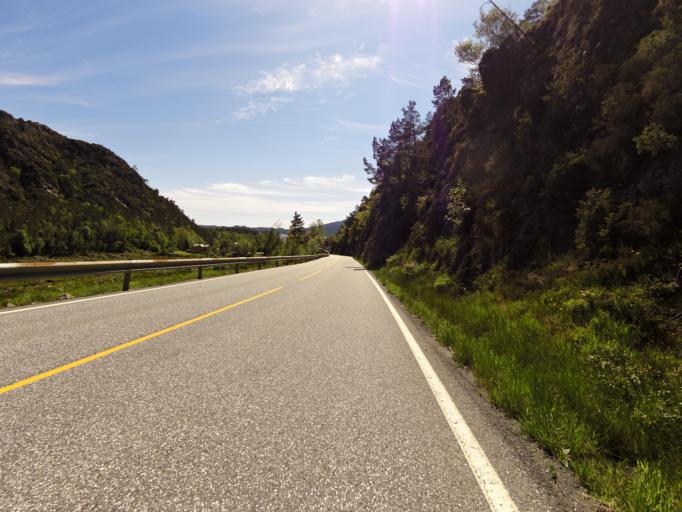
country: NO
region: Hordaland
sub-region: Stord
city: Sagvag
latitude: 59.7942
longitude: 5.3751
